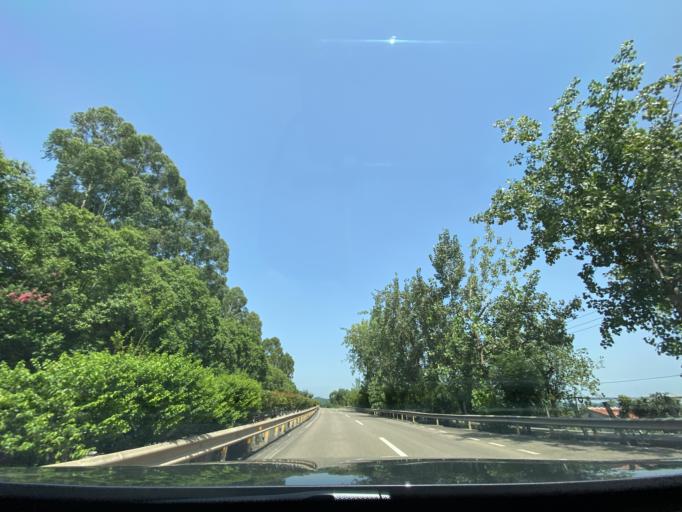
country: CN
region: Sichuan
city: Longquan
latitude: 30.4939
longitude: 104.3890
